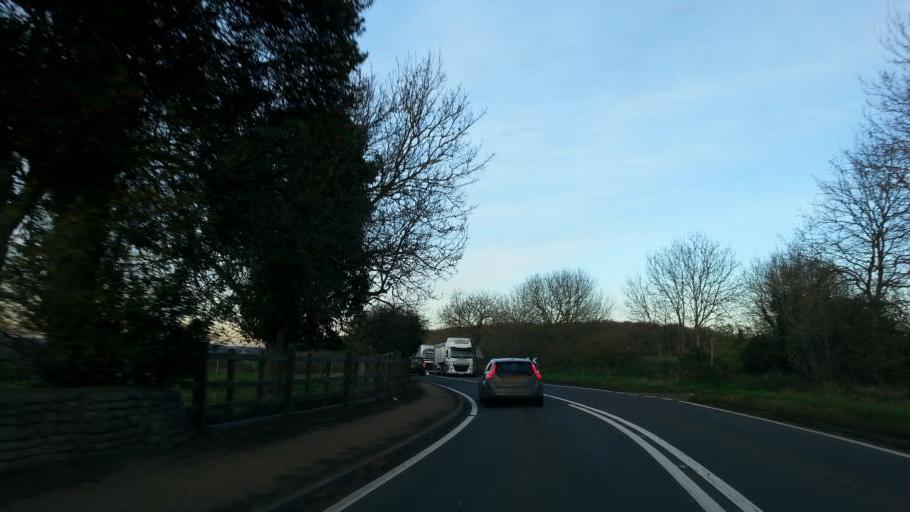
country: GB
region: England
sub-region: District of Rutland
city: Tinwell
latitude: 52.6277
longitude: -0.4991
